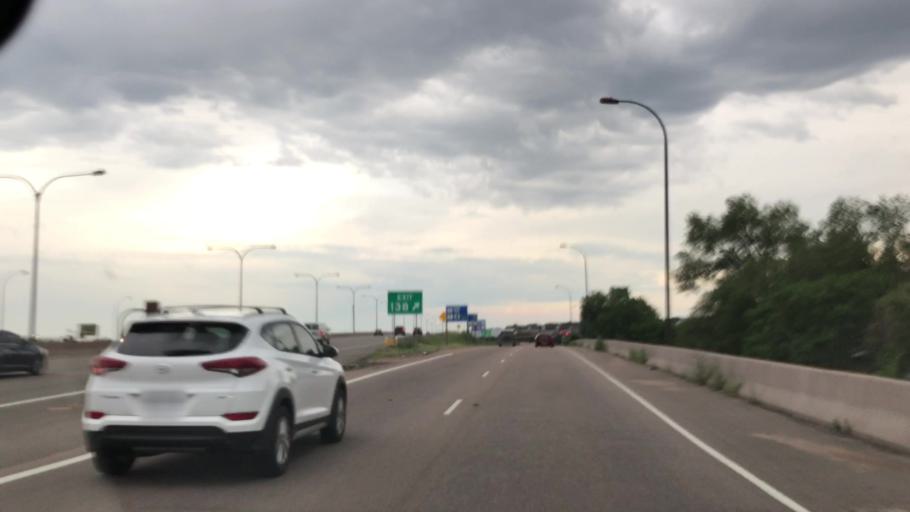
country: US
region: Colorado
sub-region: El Paso County
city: Stratmoor
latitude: 38.7990
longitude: -104.7992
